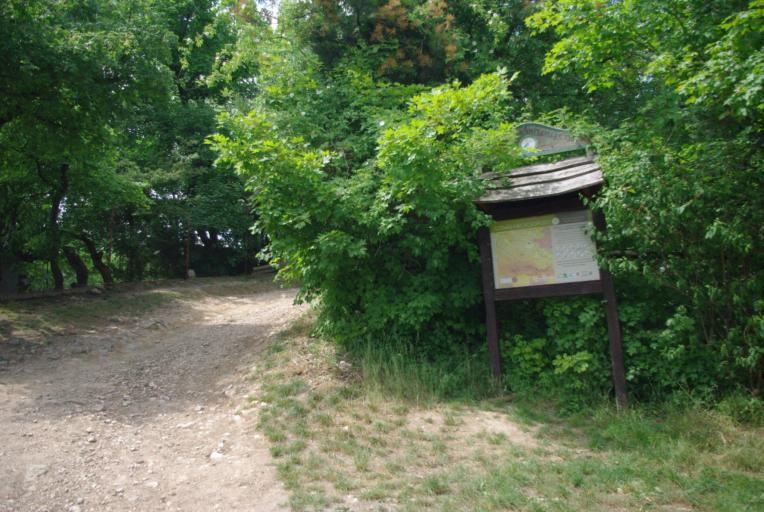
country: HU
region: Pest
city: Pilisszentivan
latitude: 47.5883
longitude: 18.8834
